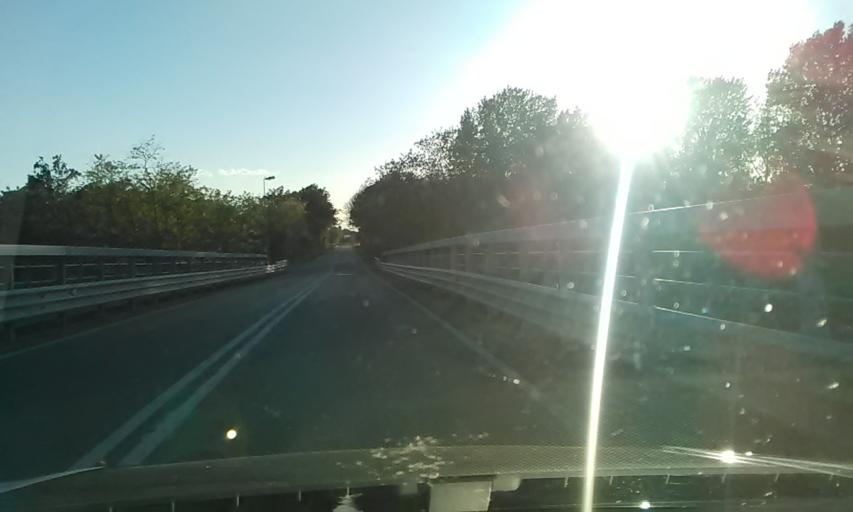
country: IT
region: Piedmont
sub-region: Provincia di Vercelli
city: Ghislarengo
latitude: 45.5300
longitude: 8.3953
